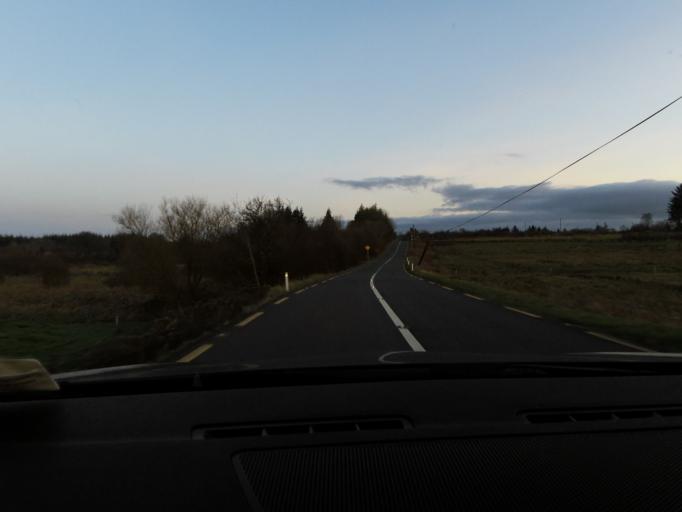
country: IE
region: Connaught
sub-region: Roscommon
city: Boyle
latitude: 53.8960
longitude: -8.2513
